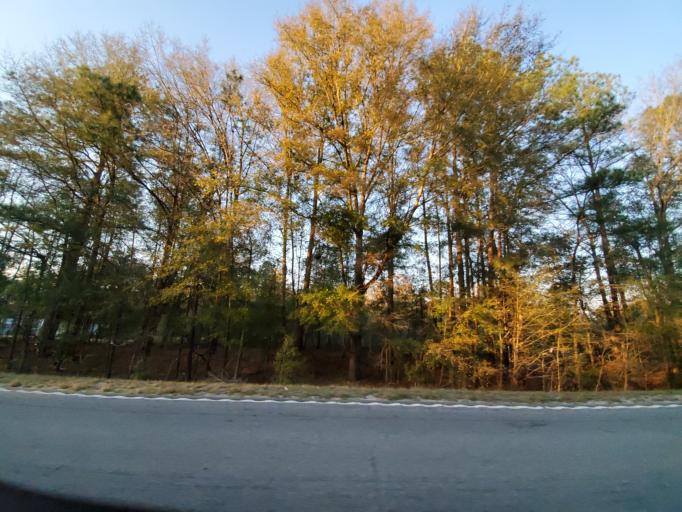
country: US
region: South Carolina
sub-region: Dorchester County
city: Ridgeville
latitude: 33.0506
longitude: -80.4645
